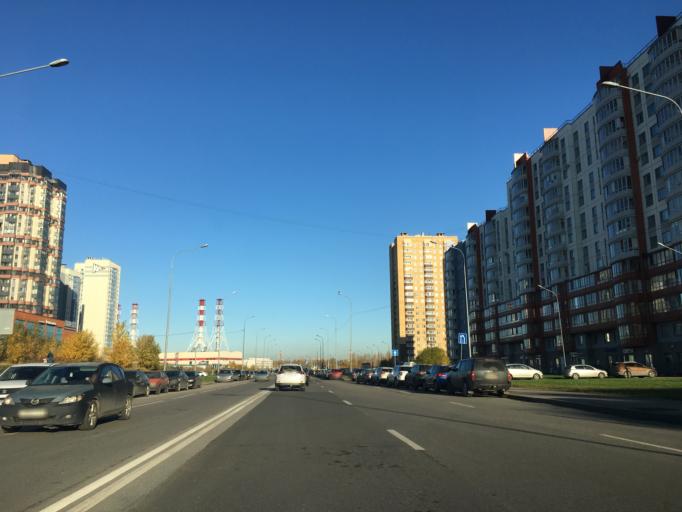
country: RU
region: St.-Petersburg
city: Uritsk
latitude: 59.8617
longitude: 30.1799
